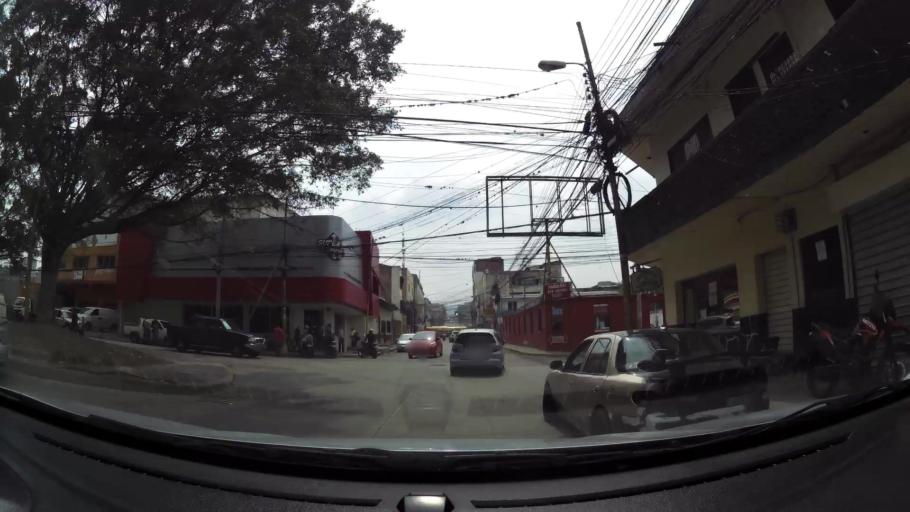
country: HN
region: Francisco Morazan
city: Tegucigalpa
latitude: 14.0928
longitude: -87.2092
